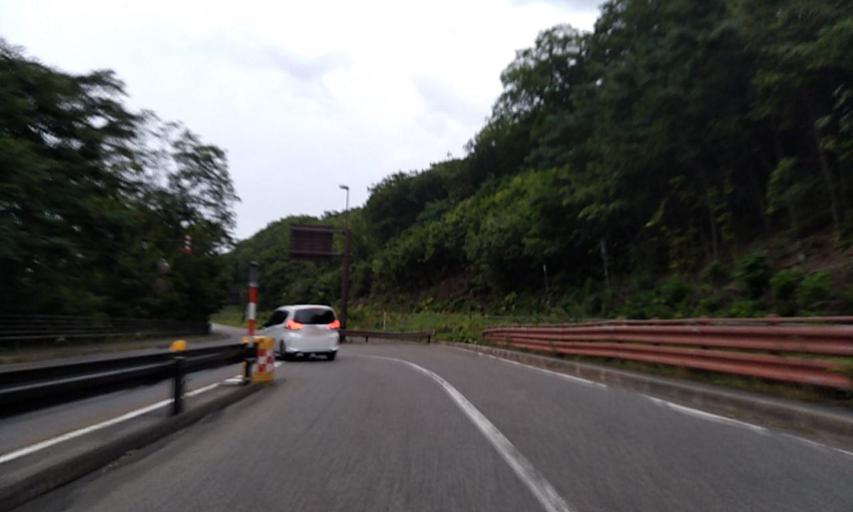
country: JP
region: Hokkaido
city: Abashiri
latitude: 44.0048
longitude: 144.2311
